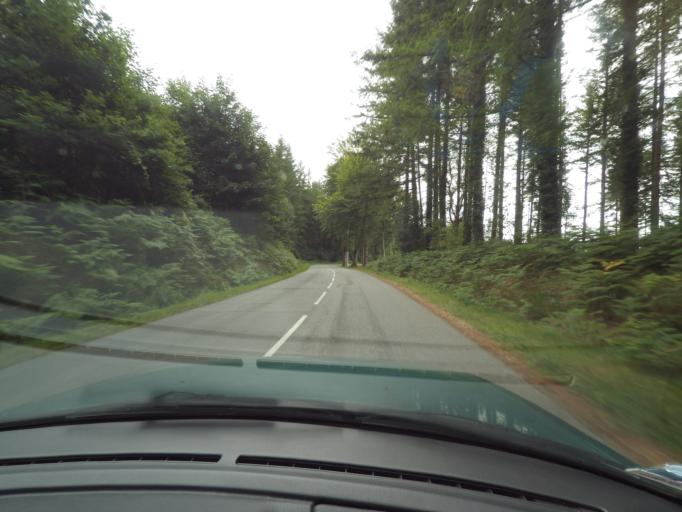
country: FR
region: Limousin
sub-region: Departement de la Haute-Vienne
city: Eymoutiers
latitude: 45.7285
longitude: 1.7838
